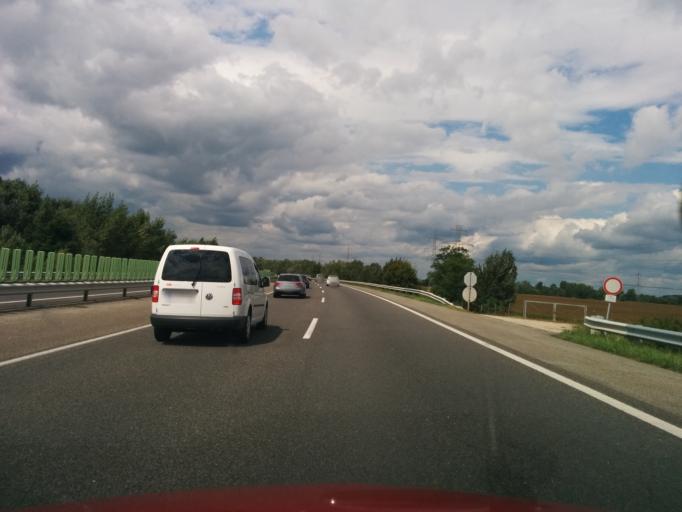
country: HU
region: Gyor-Moson-Sopron
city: Abda
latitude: 47.6854
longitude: 17.5376
